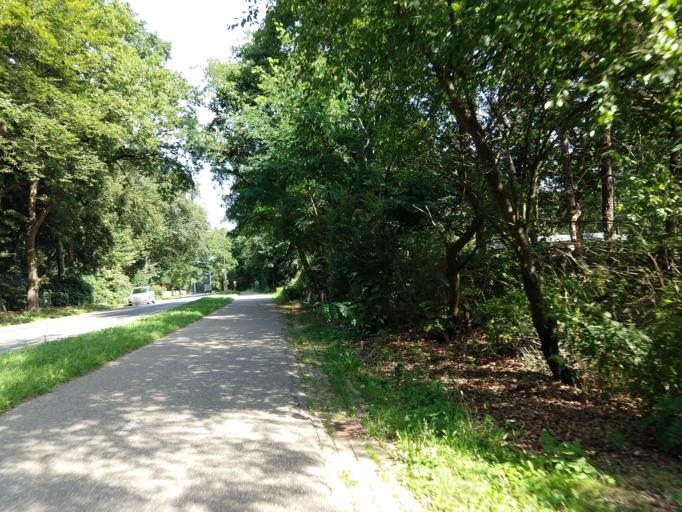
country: NL
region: Gelderland
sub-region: Gemeente Ede
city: Otterlo
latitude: 52.1072
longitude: 5.7689
